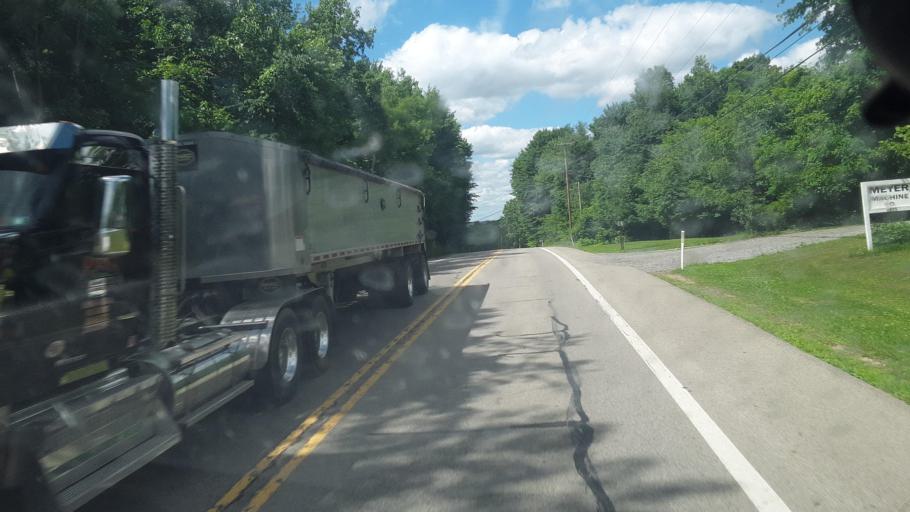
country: US
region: Pennsylvania
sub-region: Butler County
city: Slippery Rock
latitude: 40.9957
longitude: -80.1704
